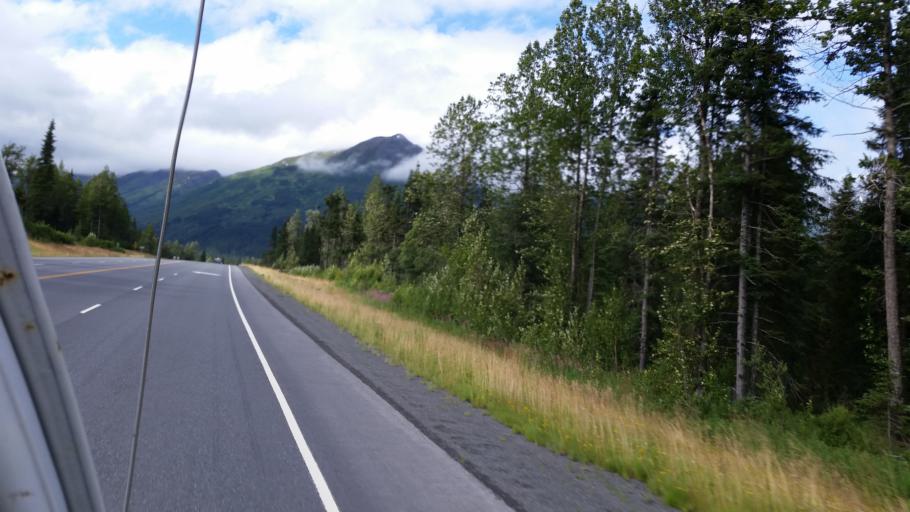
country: US
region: Alaska
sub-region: Anchorage Municipality
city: Girdwood
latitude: 60.7335
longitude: -149.2676
